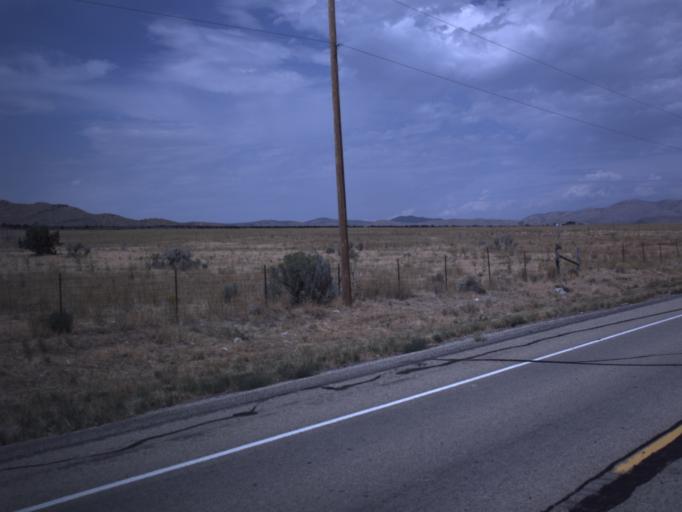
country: US
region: Utah
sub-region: Utah County
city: Eagle Mountain
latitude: 40.3356
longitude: -112.0971
